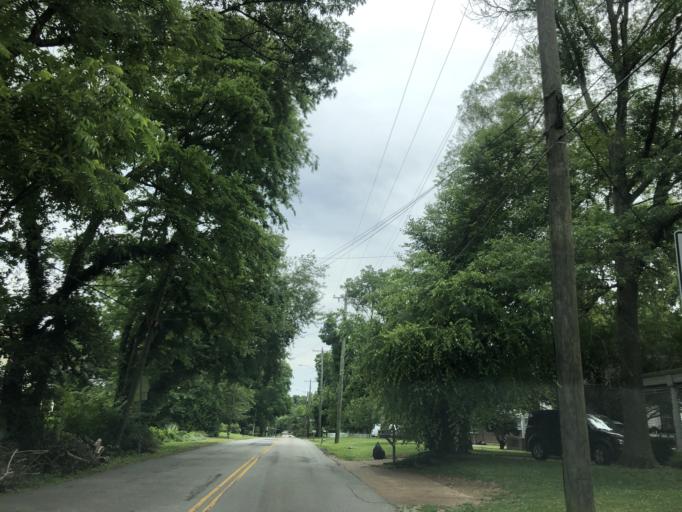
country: US
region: Tennessee
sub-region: Davidson County
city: Oak Hill
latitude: 36.1064
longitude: -86.7940
